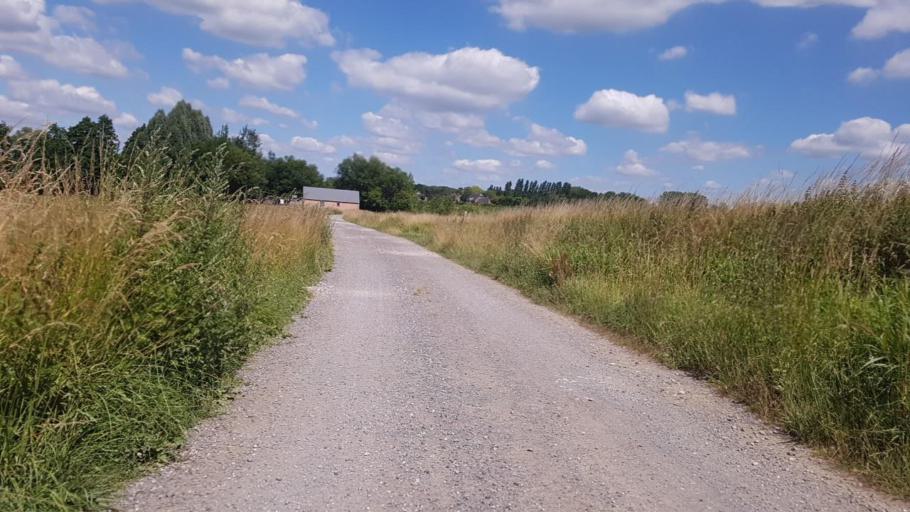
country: BE
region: Wallonia
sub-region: Province du Hainaut
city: Thuin
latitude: 50.3204
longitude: 4.3601
